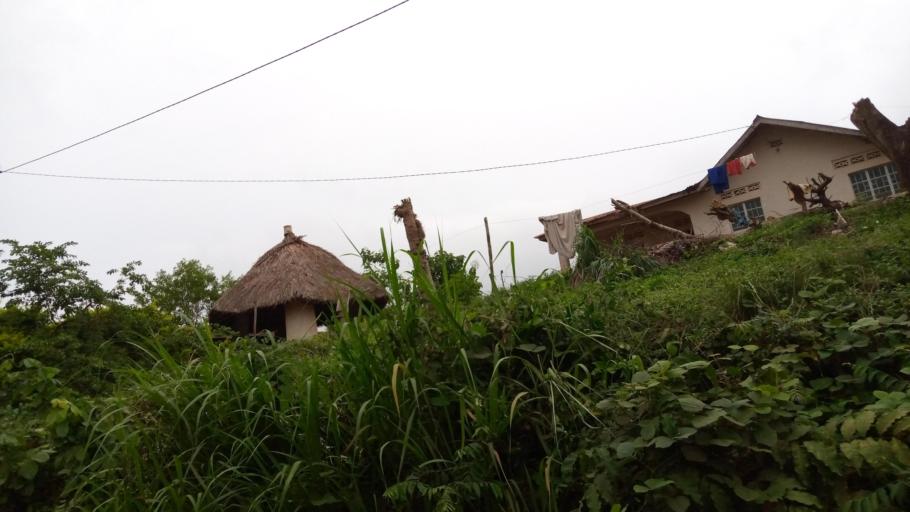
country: SL
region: Southern Province
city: Gandorhun
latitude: 7.4373
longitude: -11.8410
